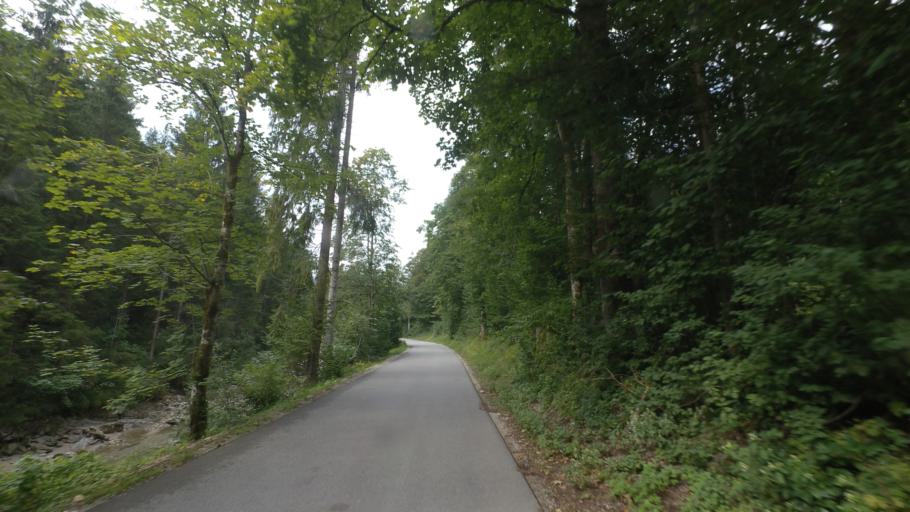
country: DE
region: Bavaria
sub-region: Upper Bavaria
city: Ruhpolding
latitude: 47.7351
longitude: 12.6003
